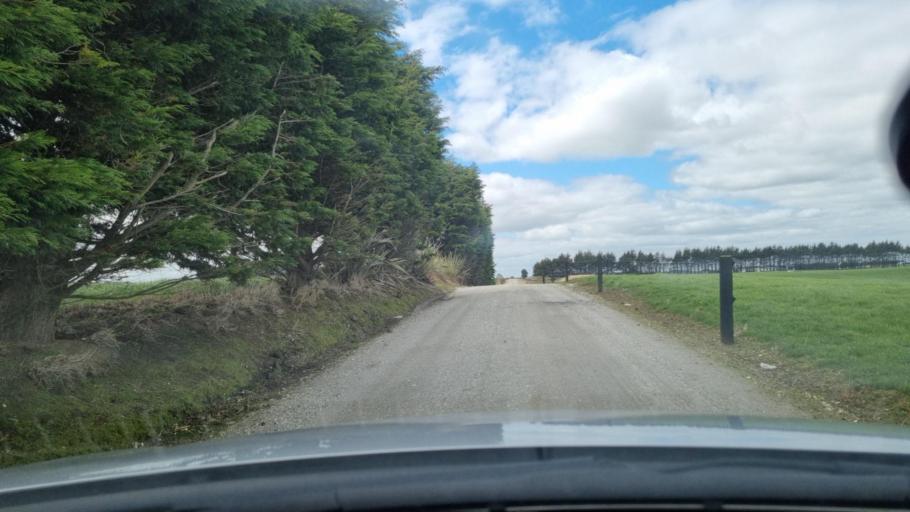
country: NZ
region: Southland
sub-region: Invercargill City
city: Invercargill
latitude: -46.4558
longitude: 168.4208
